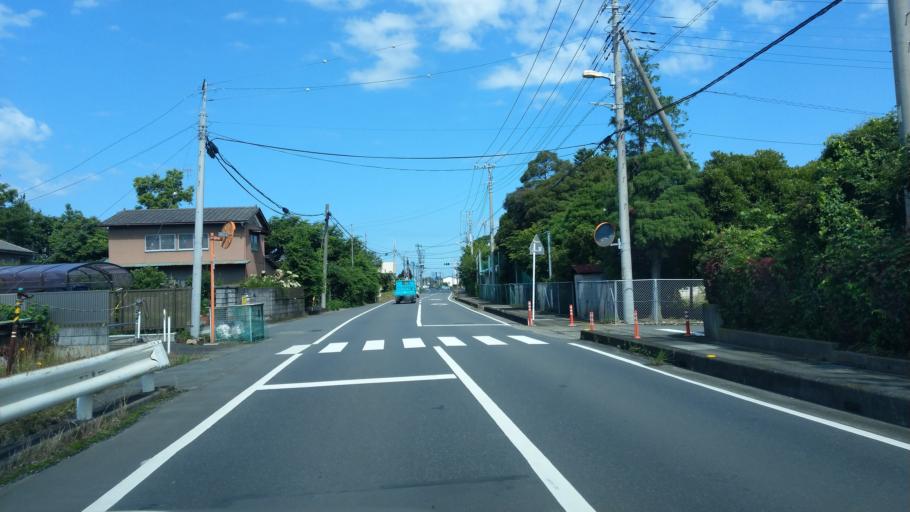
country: JP
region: Saitama
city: Kawagoe
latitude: 35.9779
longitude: 139.4905
